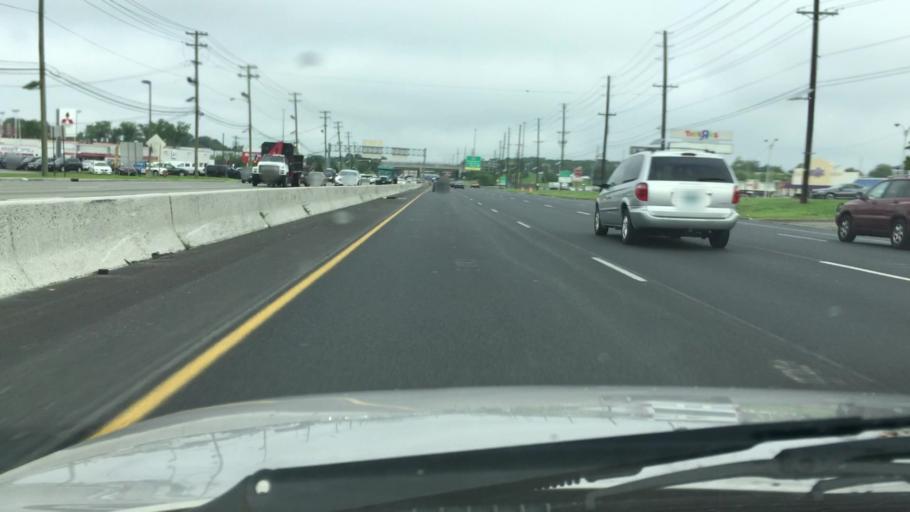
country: US
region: New Jersey
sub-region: Passaic County
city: Singac
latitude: 40.8941
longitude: -74.2304
